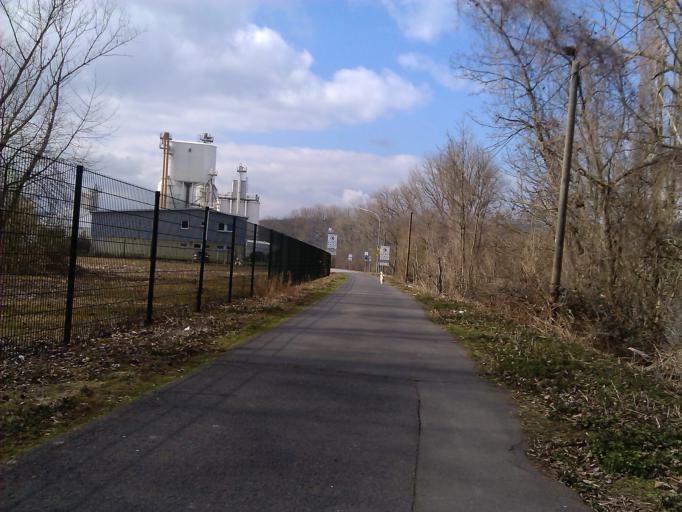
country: DE
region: Rheinland-Pfalz
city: Weissenthurm
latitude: 50.4416
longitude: 7.4343
